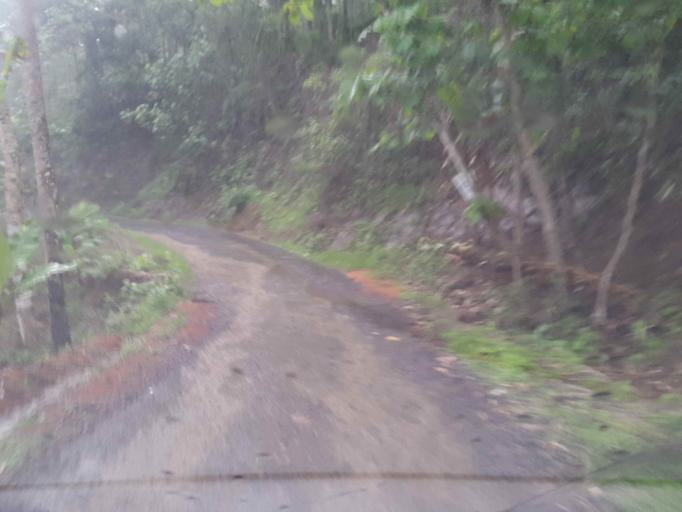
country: ID
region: Central Java
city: Bantarmangu
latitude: -7.3478
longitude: 108.8668
